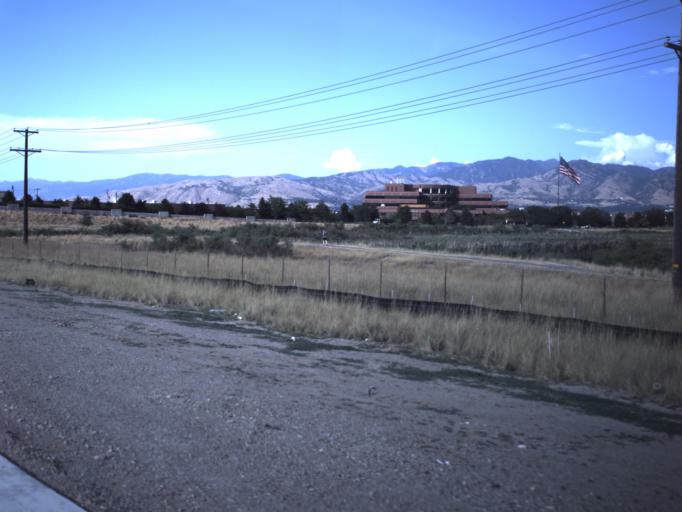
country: US
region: Utah
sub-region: Salt Lake County
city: Taylorsville
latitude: 40.7097
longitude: -111.9532
